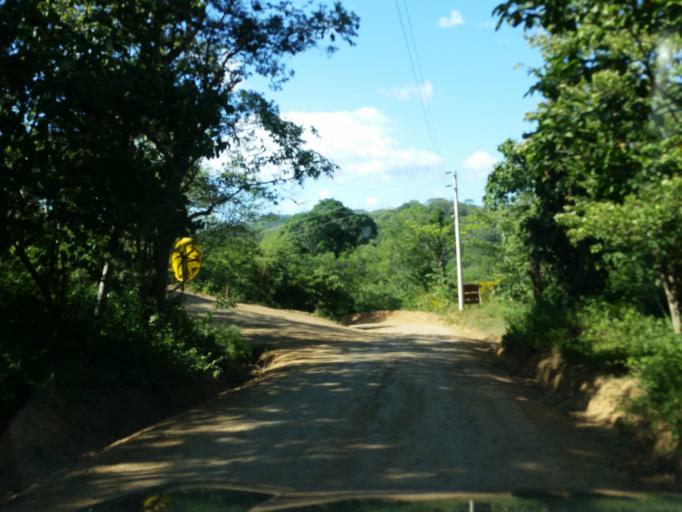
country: NI
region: Rivas
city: San Juan del Sur
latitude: 11.1845
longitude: -85.7997
